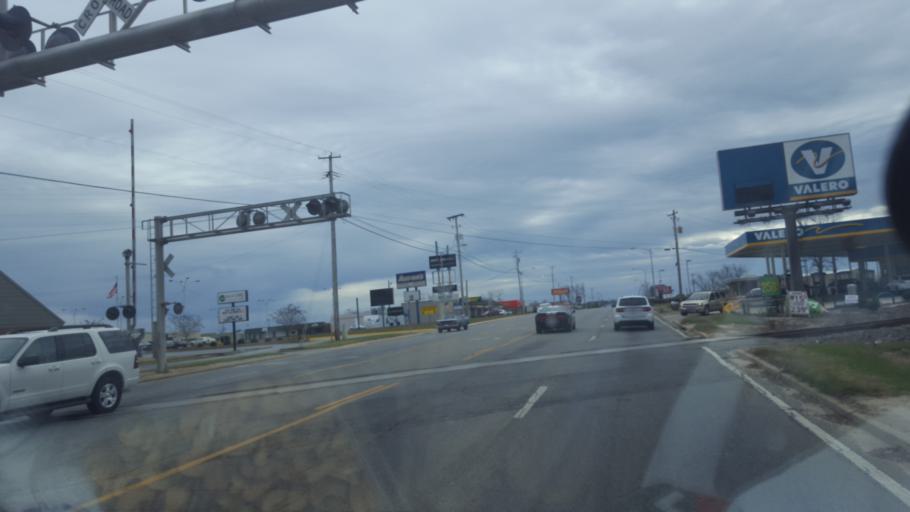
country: US
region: Georgia
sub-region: Ben Hill County
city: Fitzgerald
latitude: 31.7016
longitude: -83.2518
